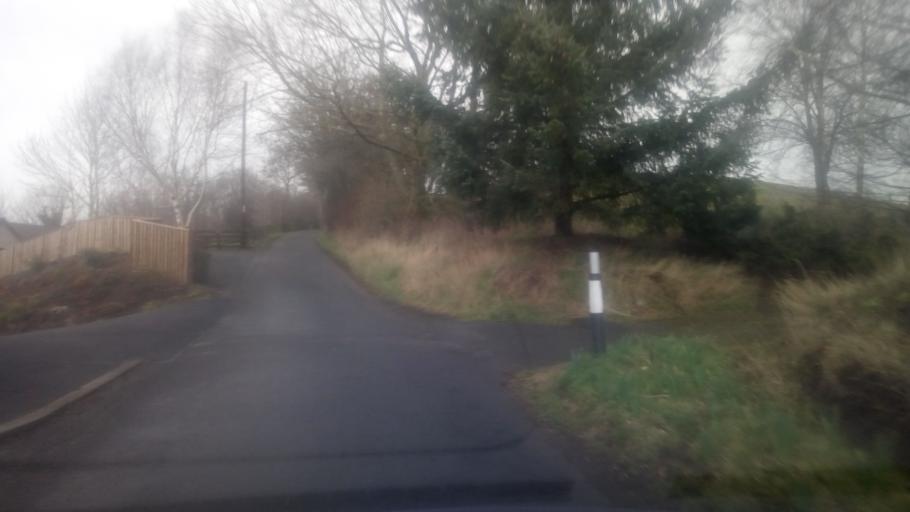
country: GB
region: Scotland
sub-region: The Scottish Borders
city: Jedburgh
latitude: 55.4898
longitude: -2.5413
